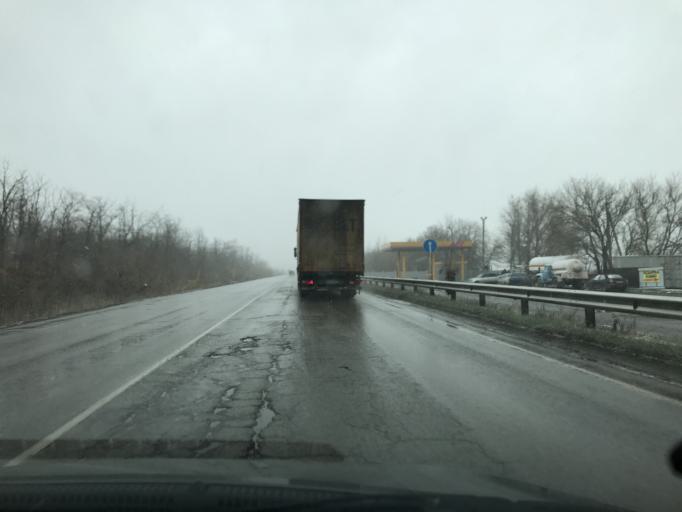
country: RU
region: Rostov
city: Bataysk
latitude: 47.0648
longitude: 39.8079
